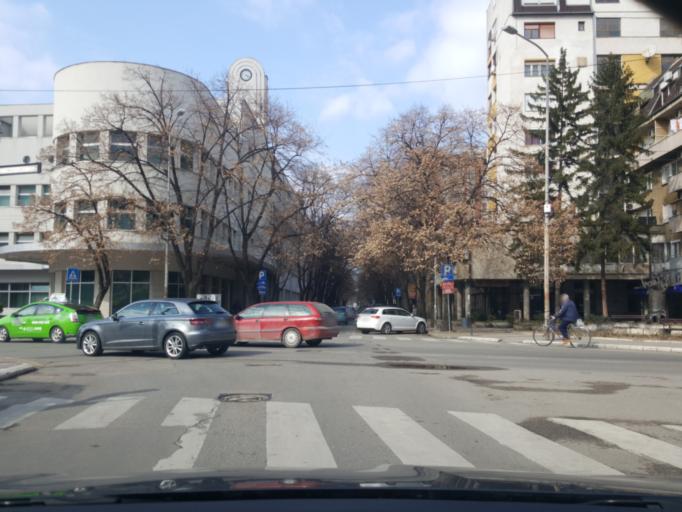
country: RS
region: Central Serbia
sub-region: Nisavski Okrug
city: Nis
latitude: 43.3178
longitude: 21.8976
